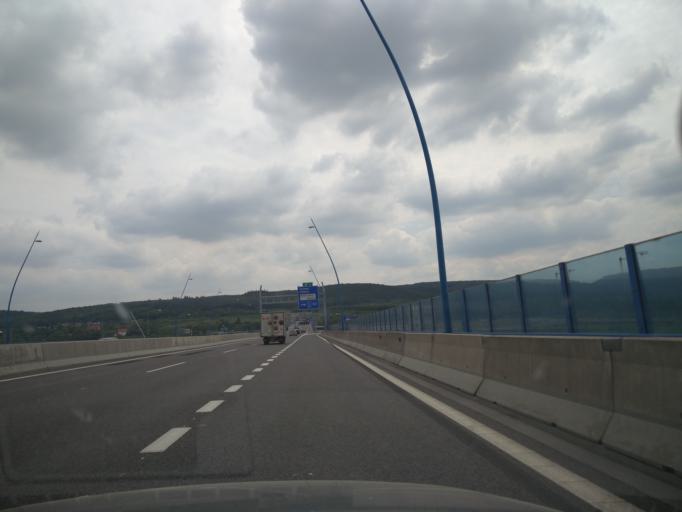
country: CZ
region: Praha
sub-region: Praha 12
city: Modrany
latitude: 49.9880
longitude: 14.3890
